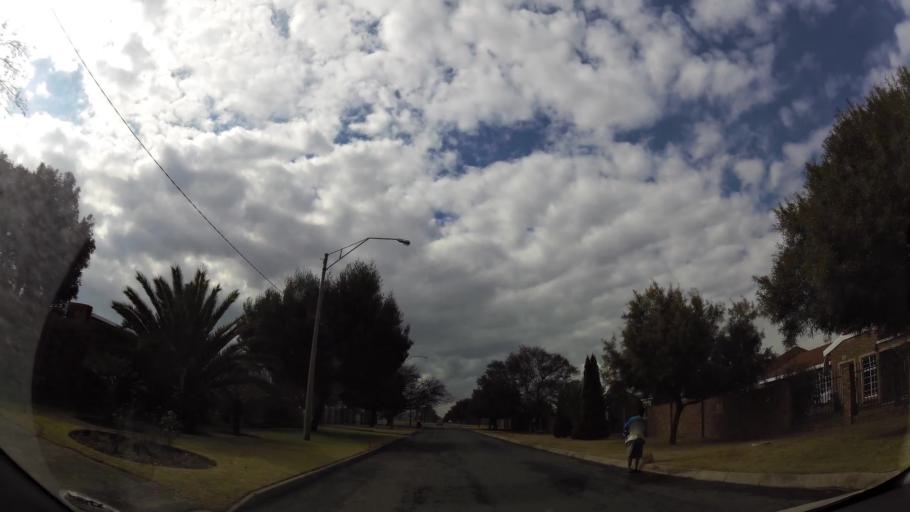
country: ZA
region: Gauteng
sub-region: Sedibeng District Municipality
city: Vereeniging
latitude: -26.6543
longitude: 27.9845
